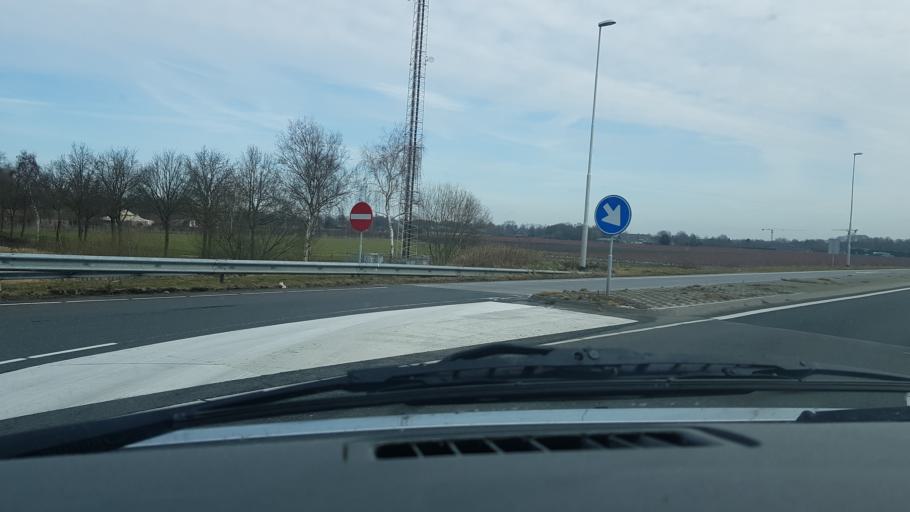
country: NL
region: North Brabant
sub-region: Gemeente Veghel
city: Mariaheide
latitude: 51.6393
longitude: 5.5679
